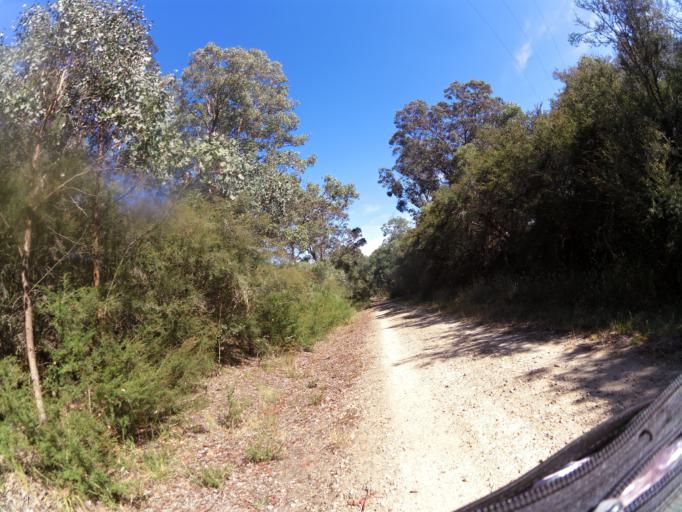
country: AU
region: Victoria
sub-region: East Gippsland
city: Lakes Entrance
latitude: -37.7373
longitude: 148.1670
